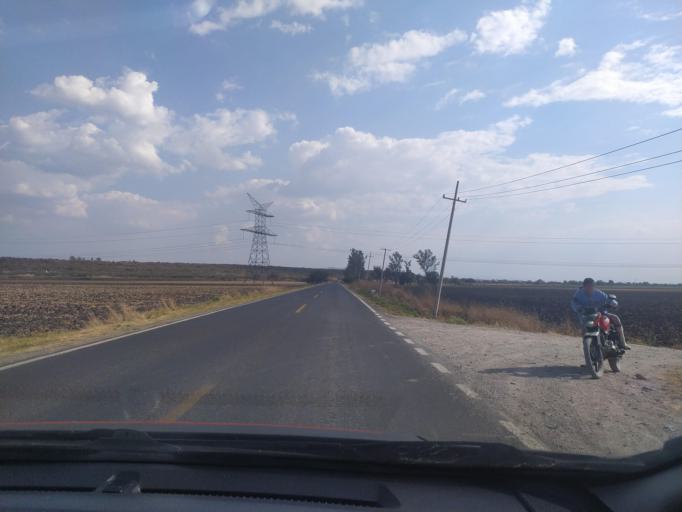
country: MX
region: Guanajuato
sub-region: San Francisco del Rincon
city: San Ignacio de Hidalgo
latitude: 20.9343
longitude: -101.8534
